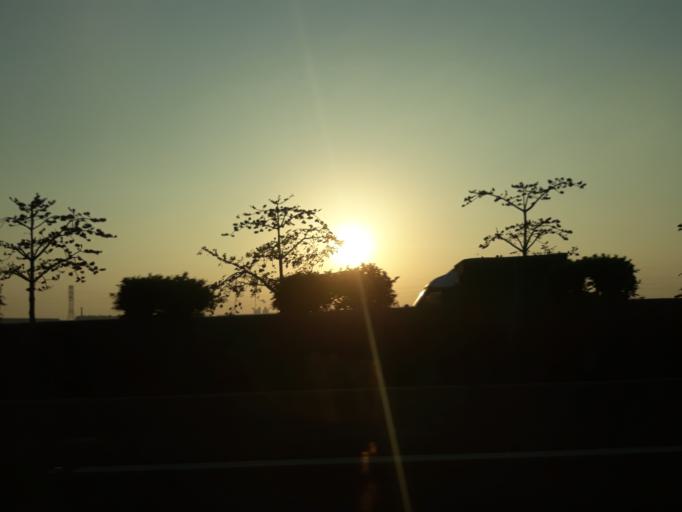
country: TW
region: Taiwan
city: Fengshan
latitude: 22.7688
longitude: 120.3277
